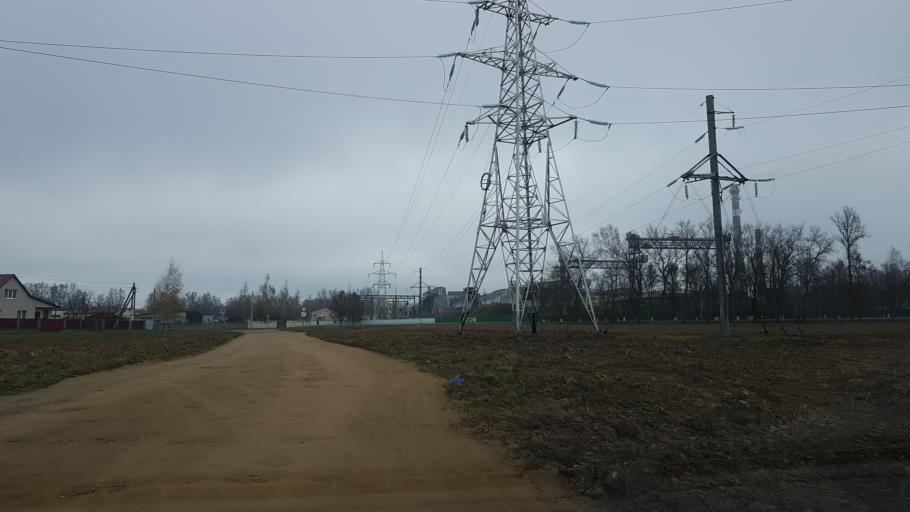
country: BY
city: Fanipol
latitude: 53.7344
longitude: 27.3241
